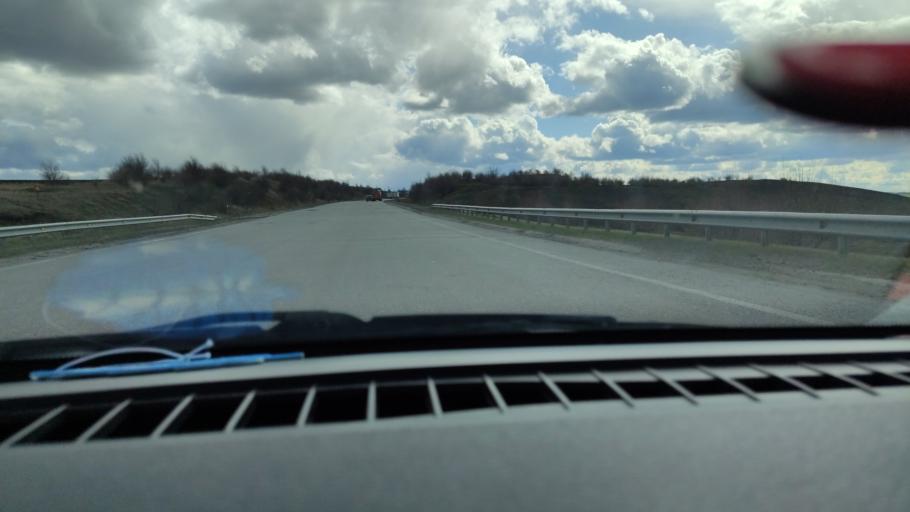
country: RU
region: Samara
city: Varlamovo
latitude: 53.0662
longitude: 48.3535
